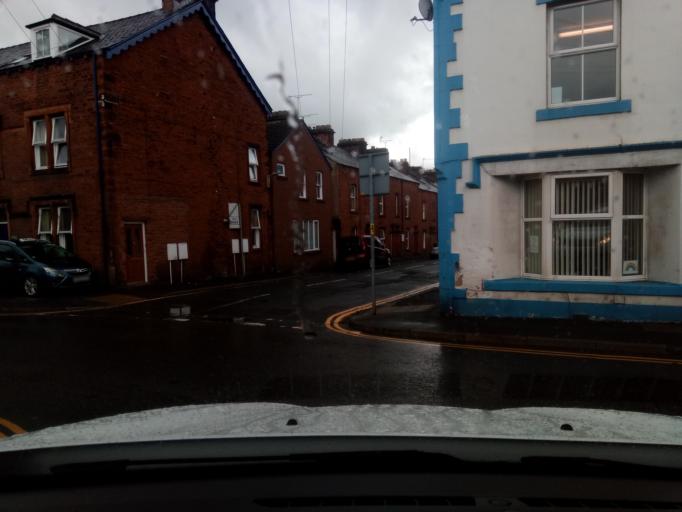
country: GB
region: England
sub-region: Cumbria
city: Penrith
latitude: 54.6668
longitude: -2.7518
